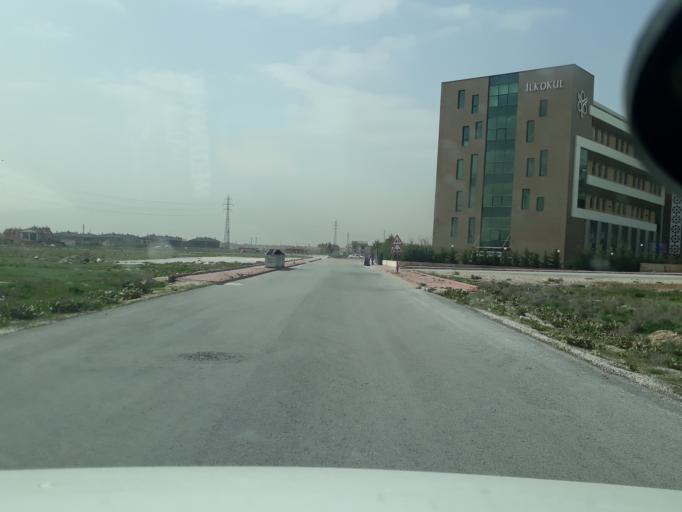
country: TR
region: Konya
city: Sille
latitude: 37.9467
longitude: 32.4756
